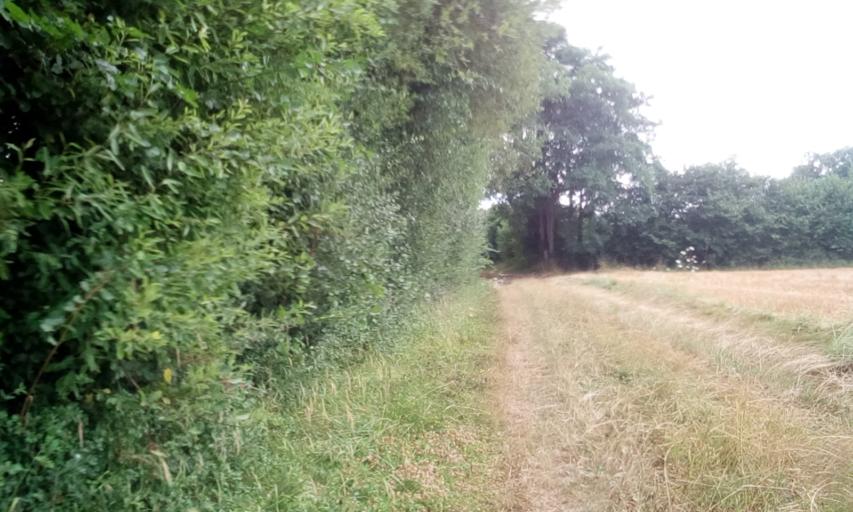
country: FR
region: Lower Normandy
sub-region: Departement du Calvados
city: Troarn
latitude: 49.1647
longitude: -0.1892
